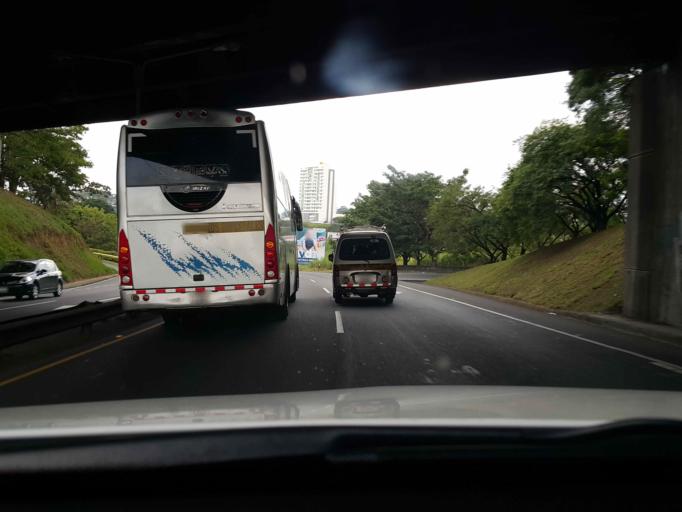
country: CR
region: San Jose
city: Colima
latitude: 9.9460
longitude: -84.1088
